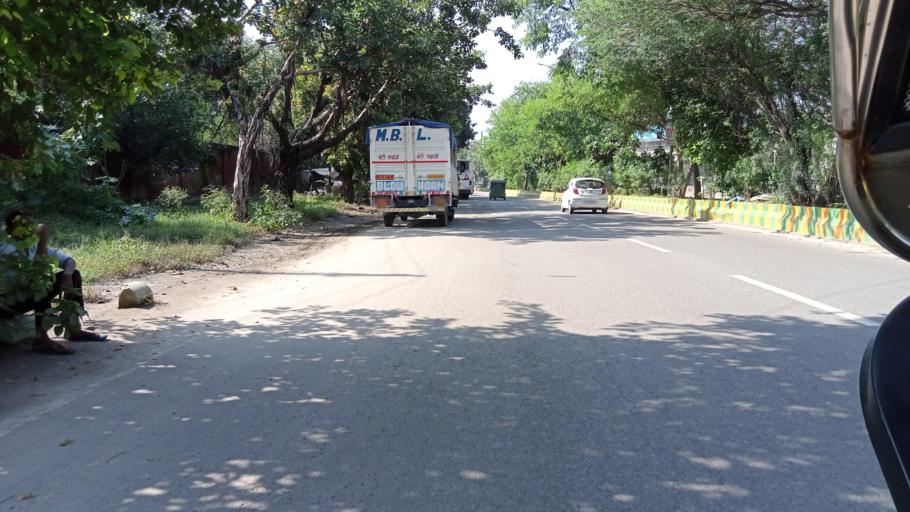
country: IN
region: Uttar Pradesh
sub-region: Ghaziabad
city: Ghaziabad
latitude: 28.6705
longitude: 77.3679
